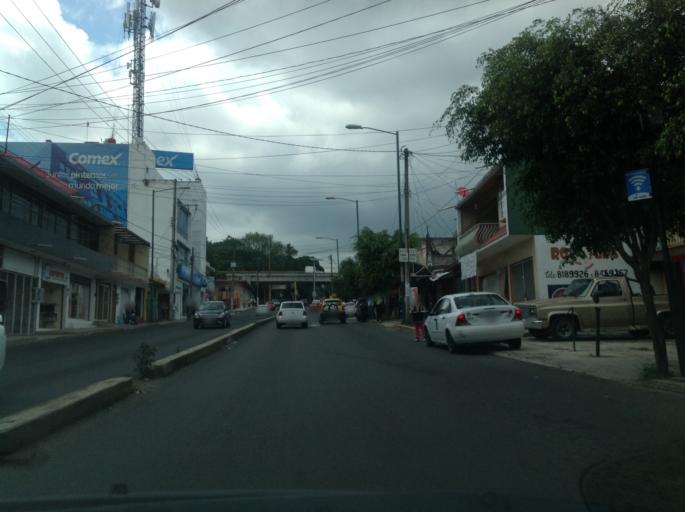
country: MX
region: Veracruz
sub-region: Xalapa
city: Xalapa de Enriquez
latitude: 19.5182
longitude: -96.9138
